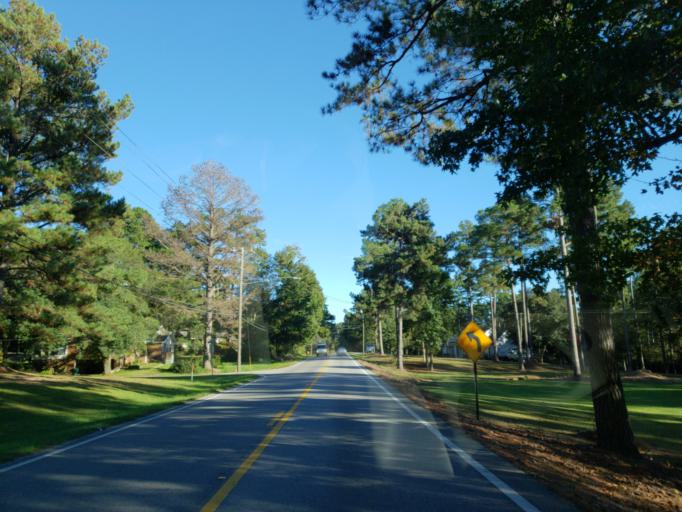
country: US
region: Mississippi
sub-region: Perry County
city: Richton
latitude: 31.3506
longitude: -88.9489
